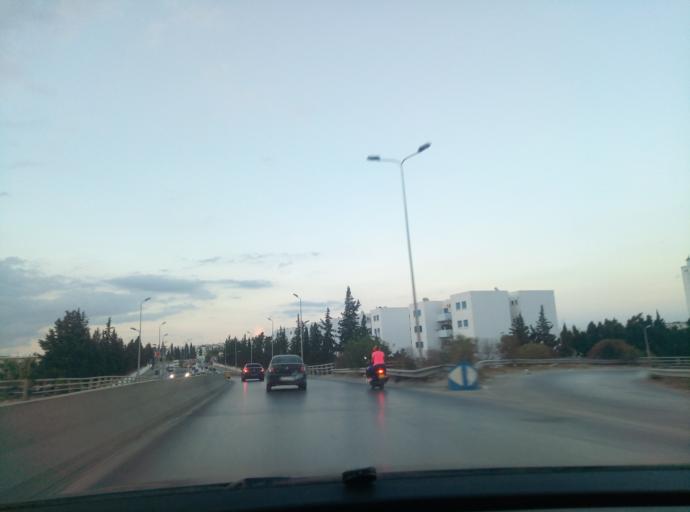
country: TN
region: Manouba
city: Manouba
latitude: 36.8108
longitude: 10.1201
